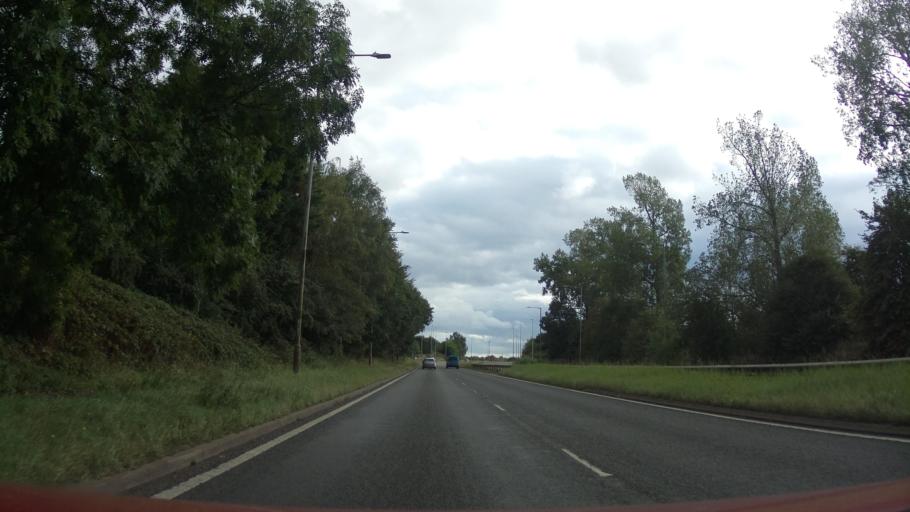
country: GB
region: England
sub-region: Solihull
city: Chelmsley Wood
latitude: 52.4858
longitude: -1.7079
